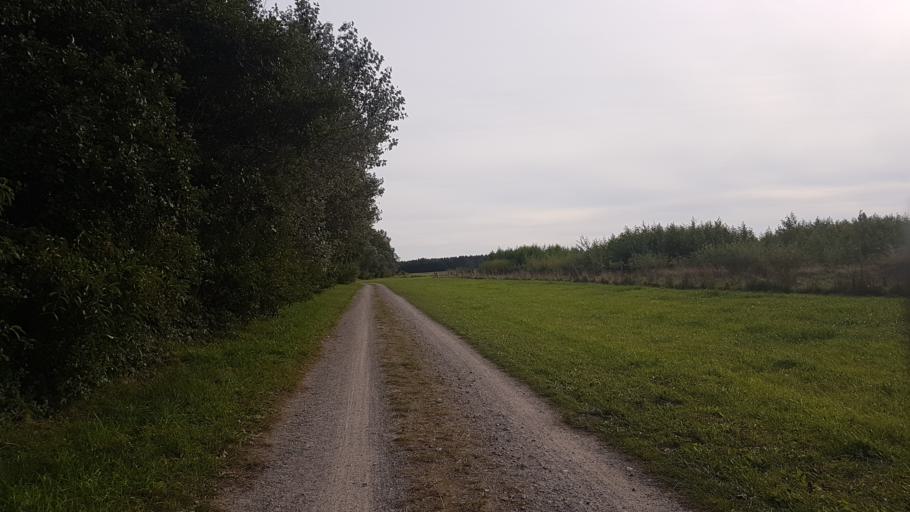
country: DE
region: Mecklenburg-Vorpommern
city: Hiddensee
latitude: 54.4862
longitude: 13.1619
